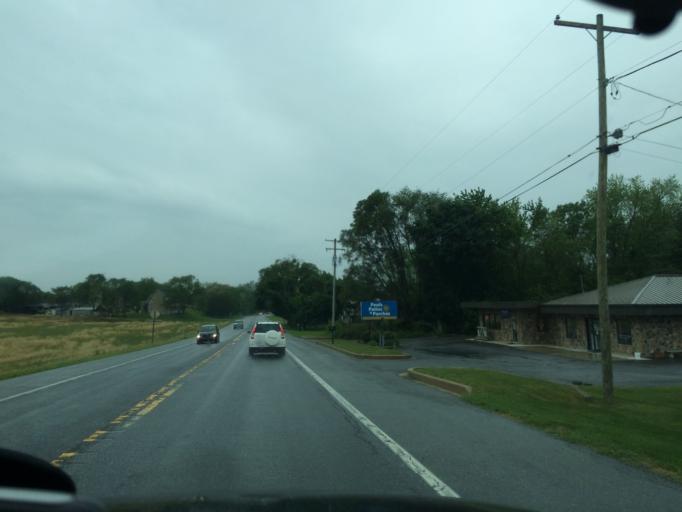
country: US
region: Maryland
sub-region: Washington County
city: Robinwood
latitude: 39.6419
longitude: -77.6363
